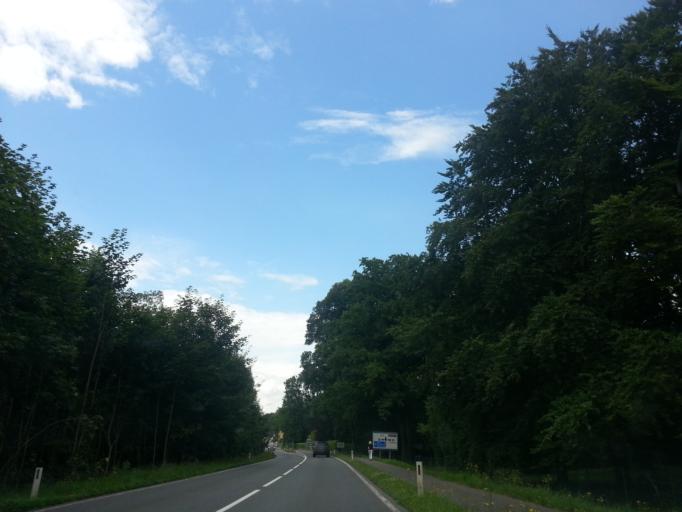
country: AT
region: Salzburg
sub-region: Politischer Bezirk Salzburg-Umgebung
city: Anif
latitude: 47.7427
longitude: 13.0683
